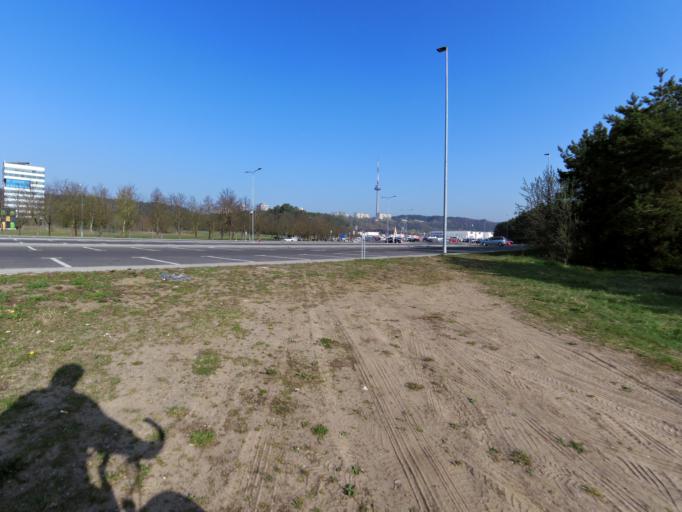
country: LT
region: Vilnius County
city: Vilkpede
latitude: 54.6746
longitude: 25.2286
